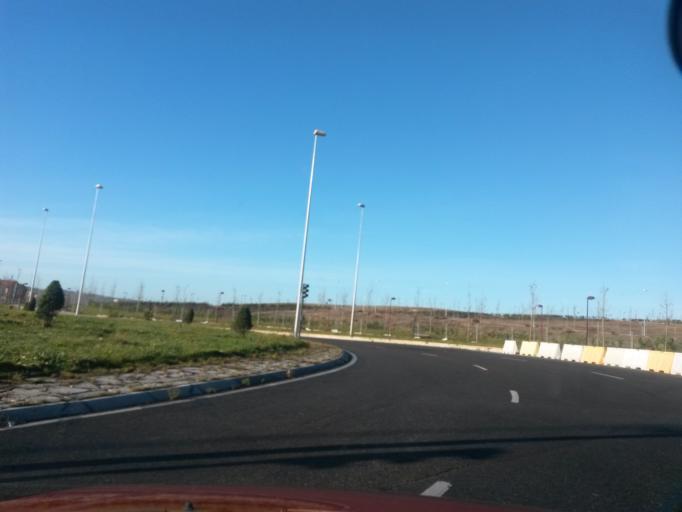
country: ES
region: Castille and Leon
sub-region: Provincia de Salamanca
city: Salamanca
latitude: 40.9679
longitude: -5.6868
